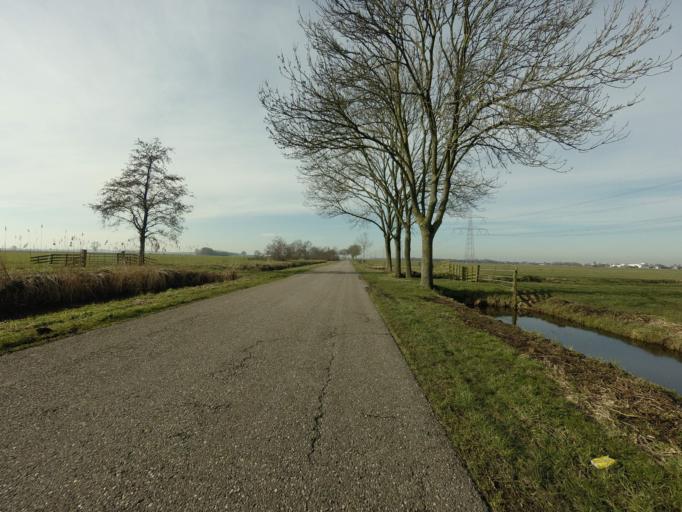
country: NL
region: South Holland
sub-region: Gemeente Sliedrecht
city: Sliedrecht
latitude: 51.8583
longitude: 4.7862
